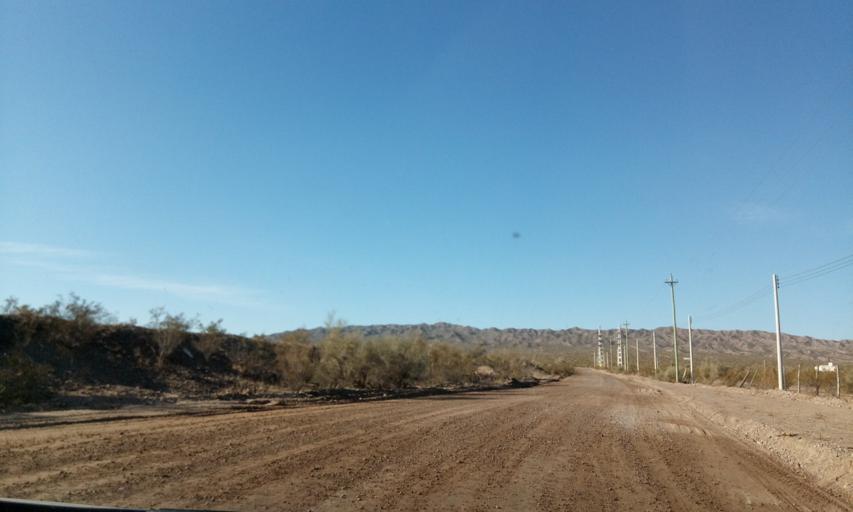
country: AR
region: San Juan
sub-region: Departamento de Rivadavia
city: Rivadavia
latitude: -31.4247
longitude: -68.6716
